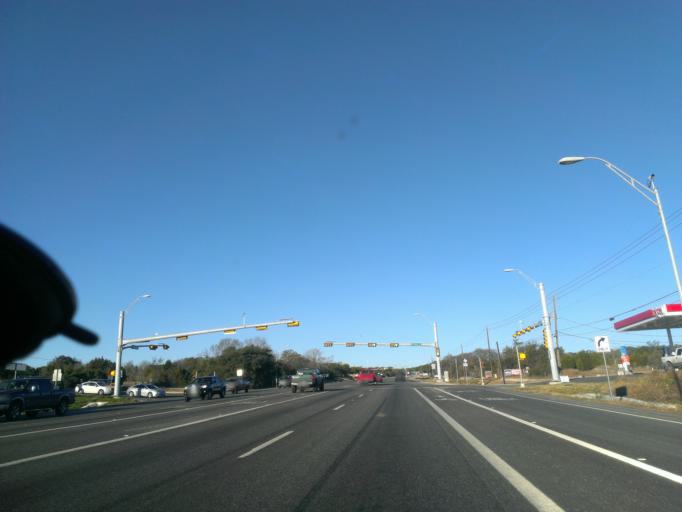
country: US
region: Texas
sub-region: Travis County
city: Barton Creek
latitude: 30.2292
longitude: -97.8871
